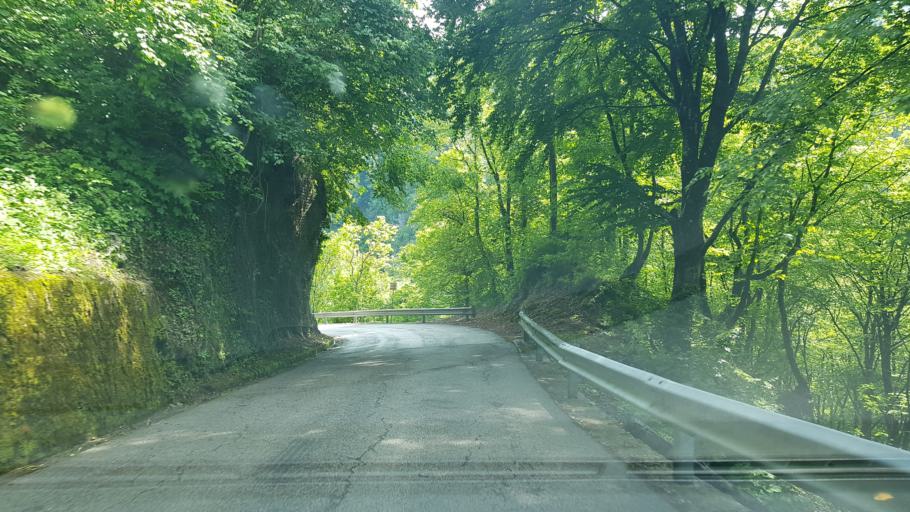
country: IT
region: Friuli Venezia Giulia
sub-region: Provincia di Udine
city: Arta Terme
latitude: 46.4680
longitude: 13.0070
